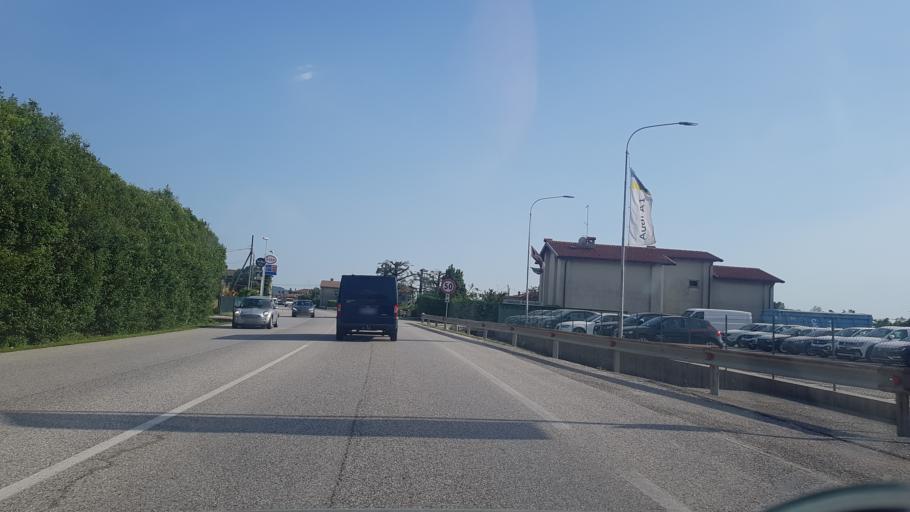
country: IT
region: Friuli Venezia Giulia
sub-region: Provincia di Udine
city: Gemona
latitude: 46.2698
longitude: 13.1075
